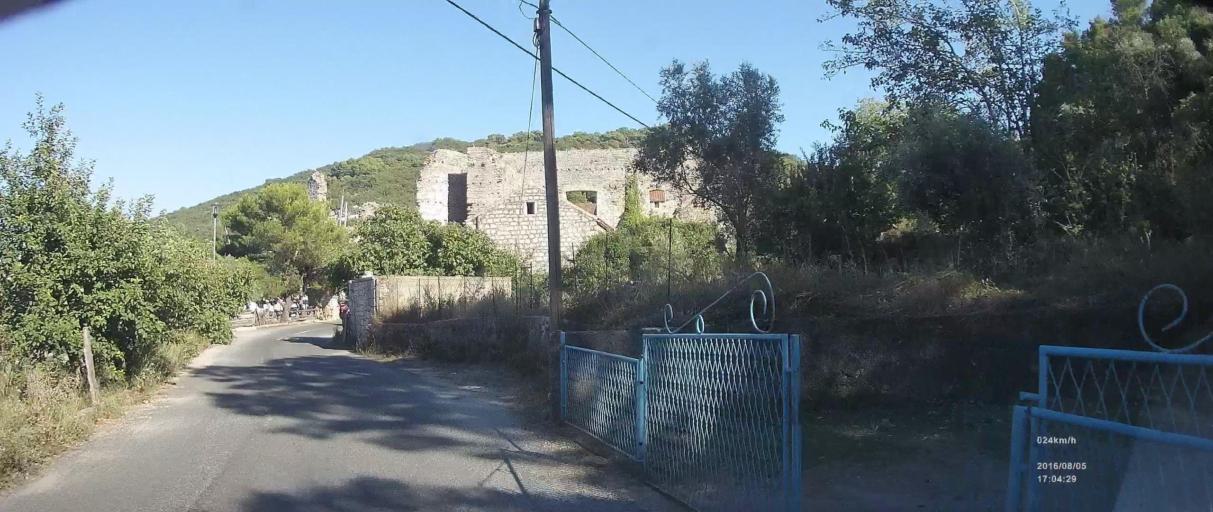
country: HR
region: Dubrovacko-Neretvanska
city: Blato
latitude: 42.7864
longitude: 17.3766
